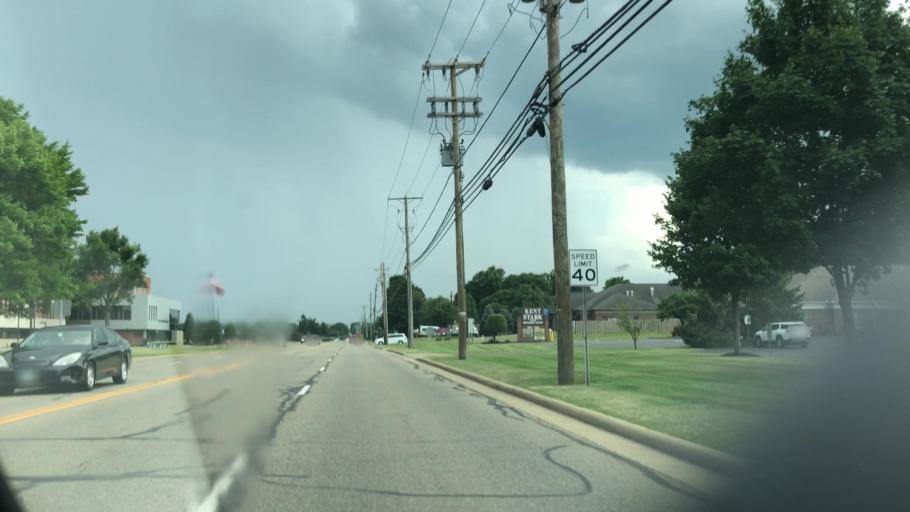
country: US
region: Ohio
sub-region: Stark County
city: North Canton
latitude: 40.8720
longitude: -81.4417
